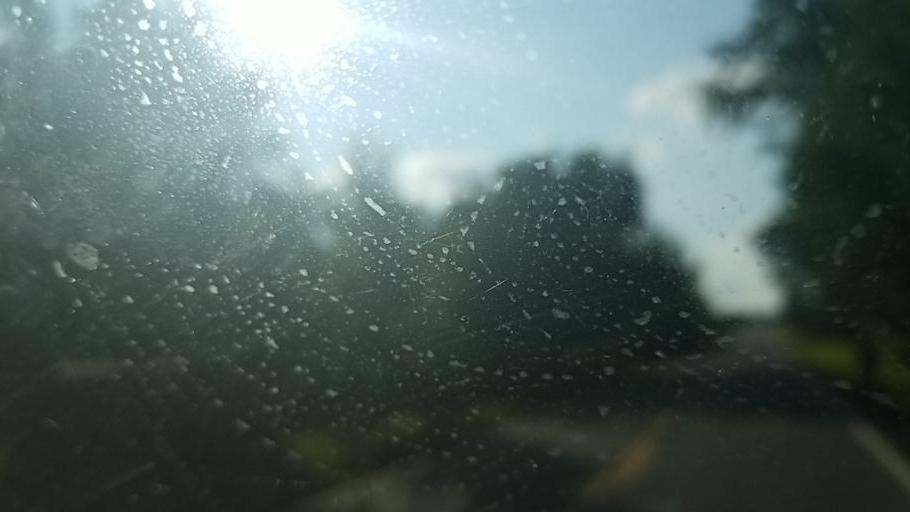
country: US
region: Ohio
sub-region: Wayne County
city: West Salem
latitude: 40.8993
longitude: -82.1600
